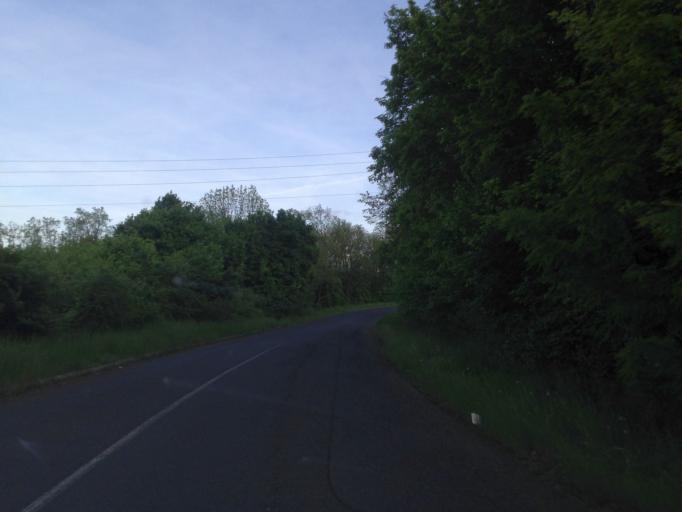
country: HU
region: Nograd
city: Tar
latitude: 47.9413
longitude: 19.7244
